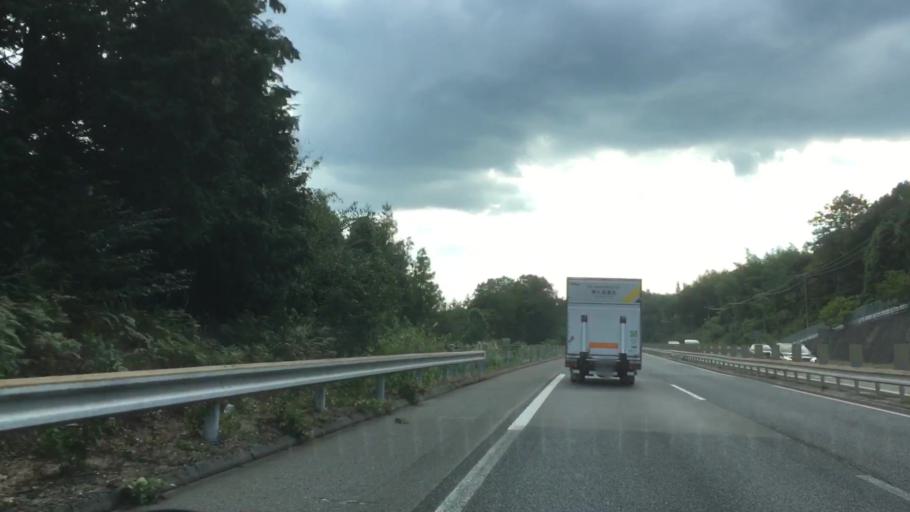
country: JP
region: Yamaguchi
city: Iwakuni
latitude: 34.1356
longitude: 132.1161
